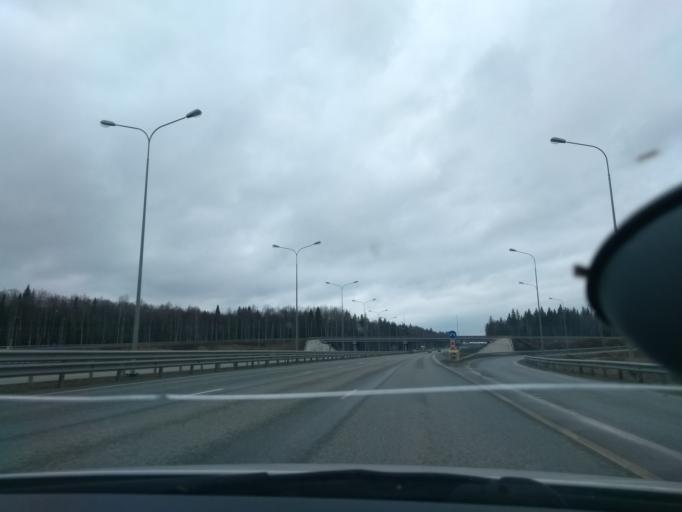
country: RU
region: Perm
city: Bershet'
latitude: 57.6975
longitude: 56.3843
